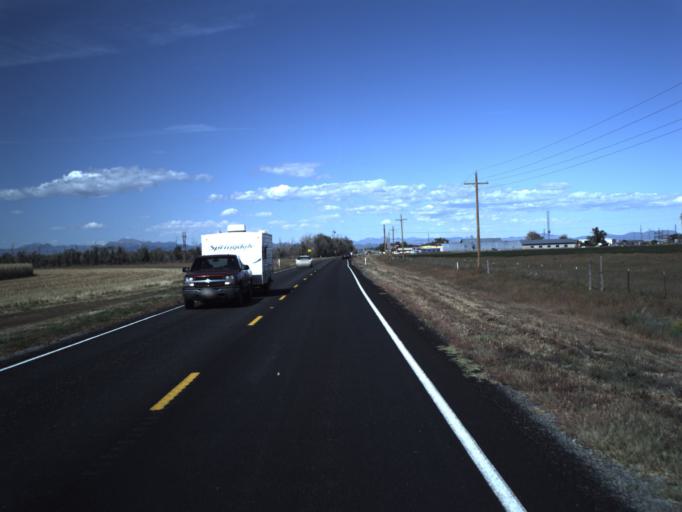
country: US
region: Utah
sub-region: Washington County
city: Enterprise
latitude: 37.7027
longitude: -113.6565
